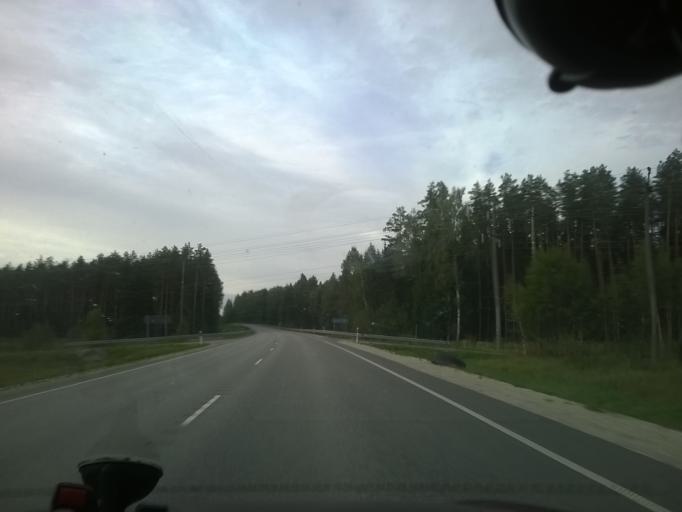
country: EE
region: Vorumaa
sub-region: Voru linn
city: Voru
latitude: 57.9626
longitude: 26.7916
